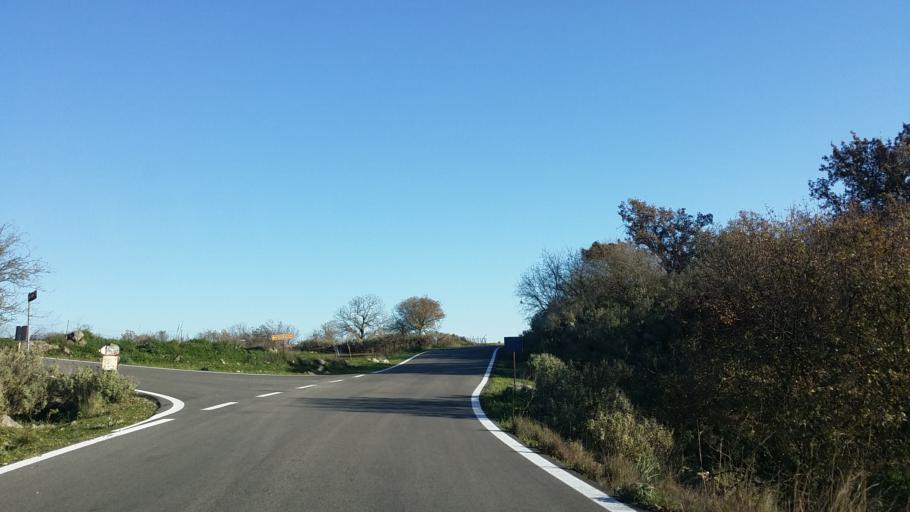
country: GR
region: West Greece
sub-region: Nomos Aitolias kai Akarnanias
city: Fitiai
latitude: 38.6352
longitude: 21.1959
